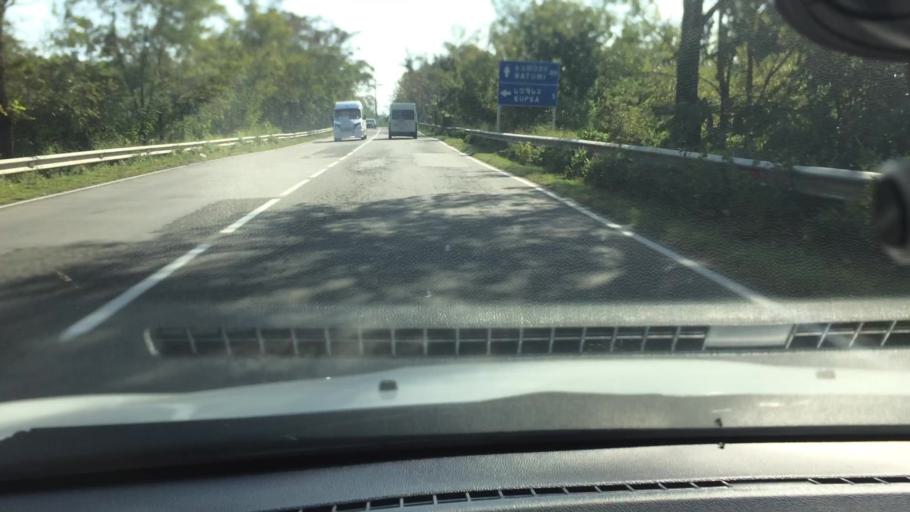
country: GE
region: Guria
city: Urek'i
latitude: 42.0129
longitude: 41.7759
